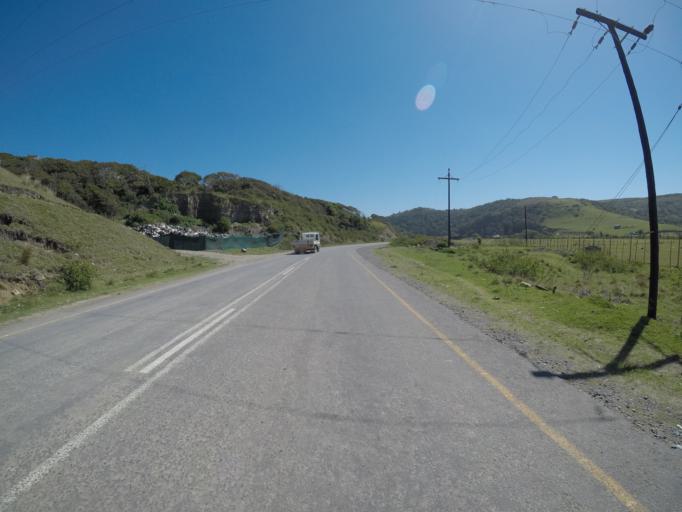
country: ZA
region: Eastern Cape
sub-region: OR Tambo District Municipality
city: Libode
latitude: -31.9826
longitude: 29.1476
